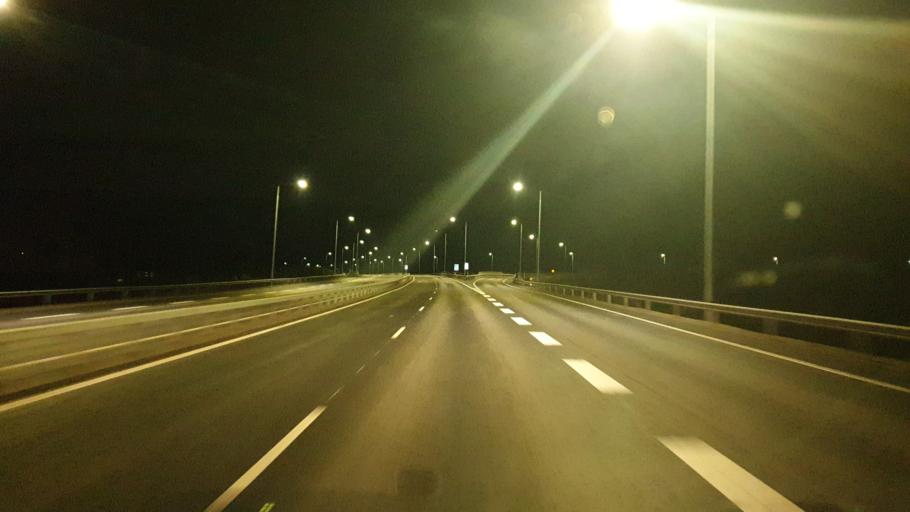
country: FI
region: Central Finland
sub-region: AEaenekoski
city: AEaenekoski
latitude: 62.6072
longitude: 25.6893
